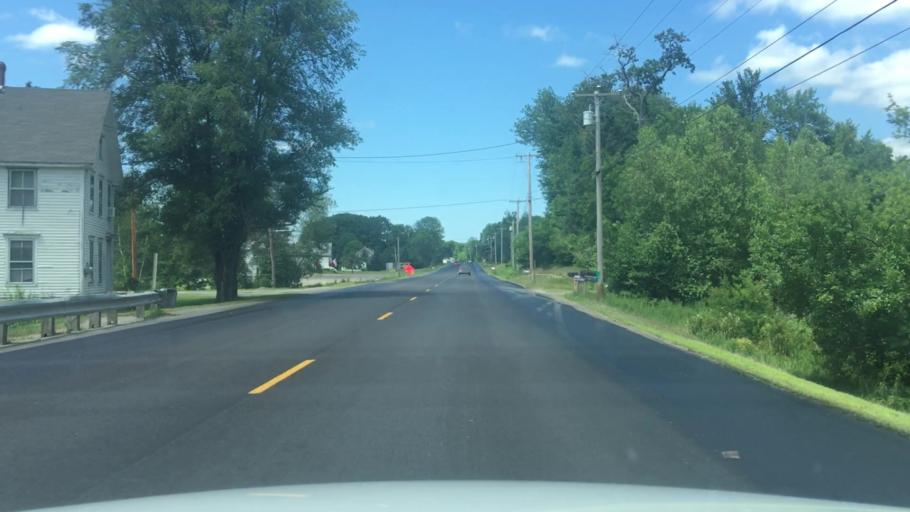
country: US
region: Maine
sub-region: Waldo County
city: Searsmont
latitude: 44.4074
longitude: -69.2085
